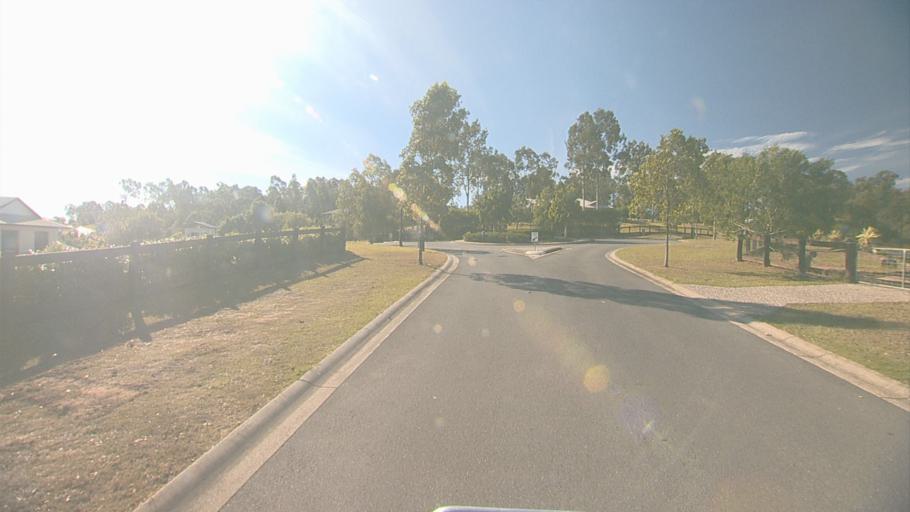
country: AU
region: Queensland
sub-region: Ipswich
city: Springfield Lakes
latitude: -27.7235
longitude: 152.9246
